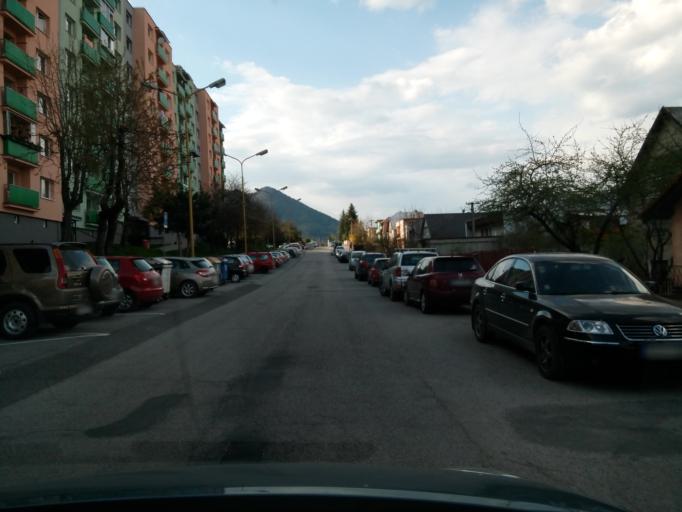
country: SK
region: Zilinsky
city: Ruzomberok
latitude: 49.0660
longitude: 19.2980
